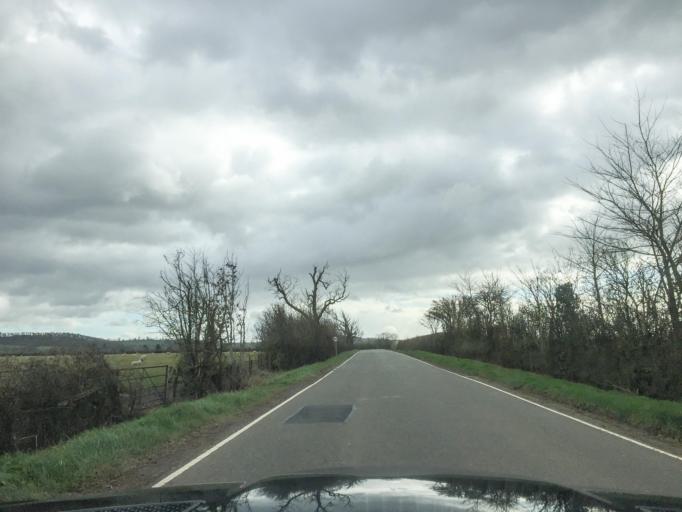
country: GB
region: England
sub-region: Warwickshire
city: Wellesbourne Mountford
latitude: 52.1149
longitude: -1.5021
